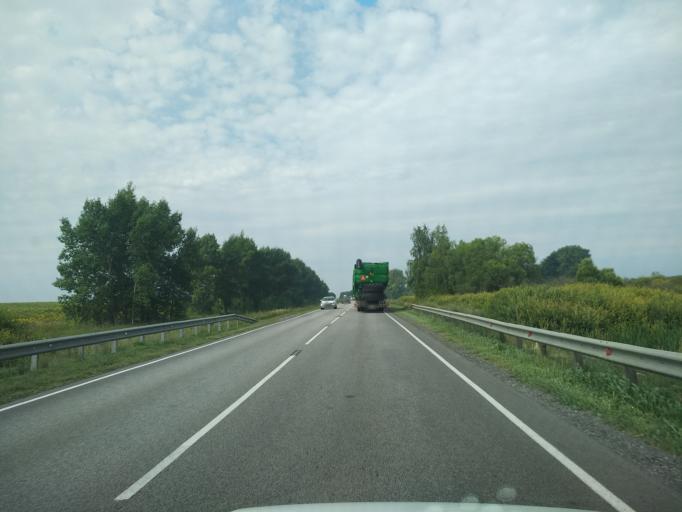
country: RU
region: Voronezj
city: Pereleshinskiy
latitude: 51.8725
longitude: 40.3951
